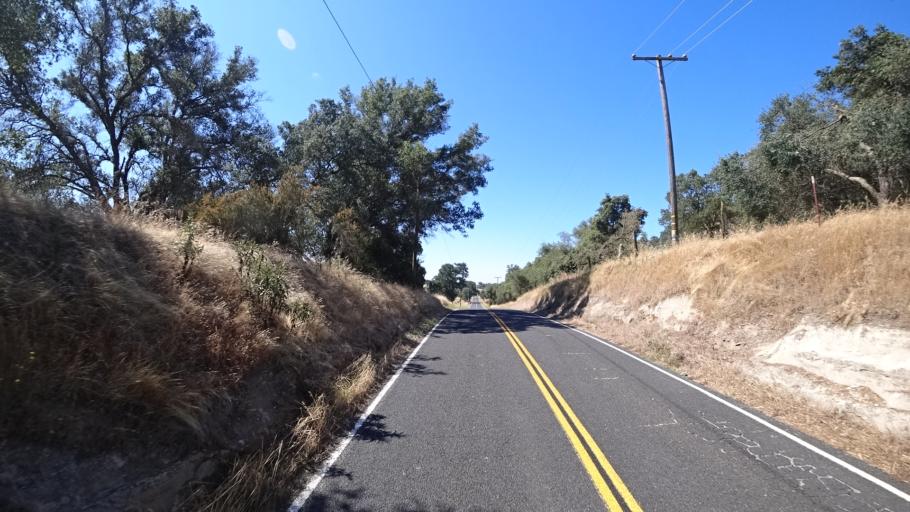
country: US
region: California
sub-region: Calaveras County
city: Rancho Calaveras
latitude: 38.1292
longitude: -120.9265
